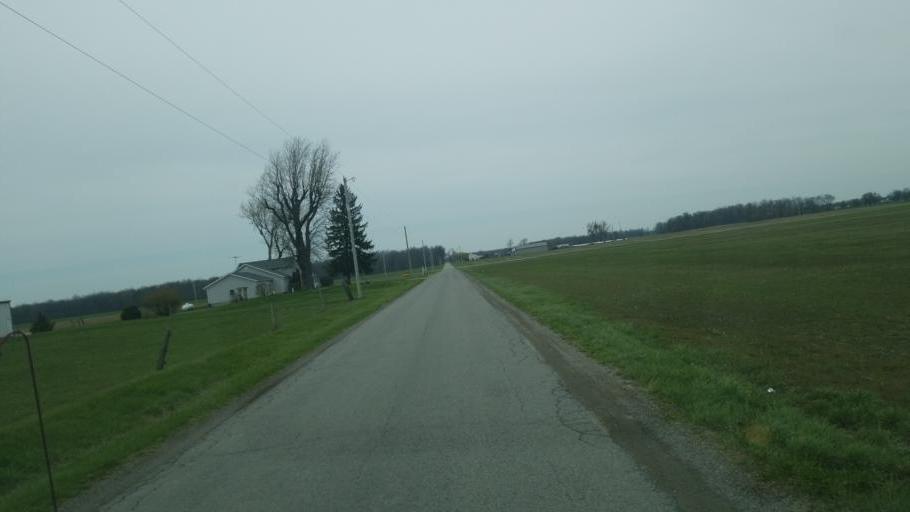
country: US
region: Ohio
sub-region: Wyandot County
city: Carey
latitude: 40.9603
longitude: -83.5131
